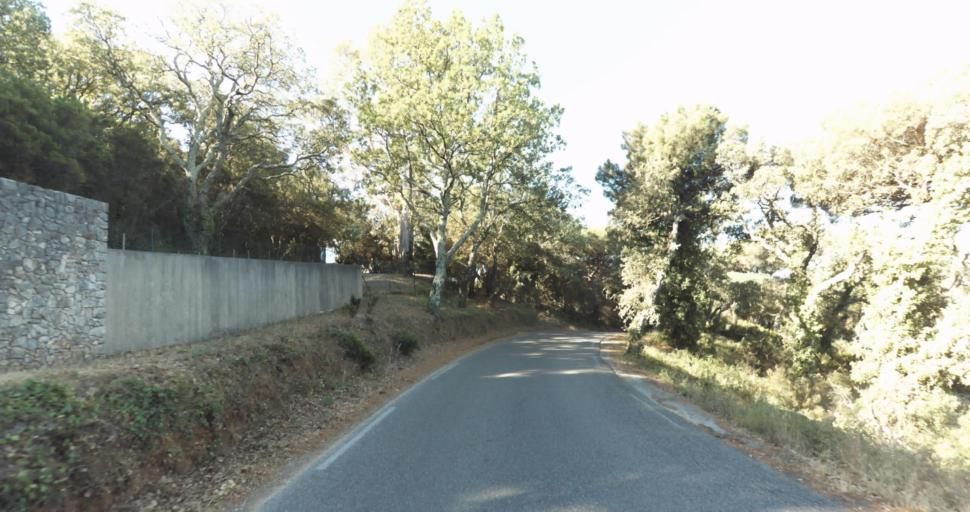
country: FR
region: Provence-Alpes-Cote d'Azur
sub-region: Departement du Var
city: Gassin
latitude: 43.2214
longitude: 6.5882
